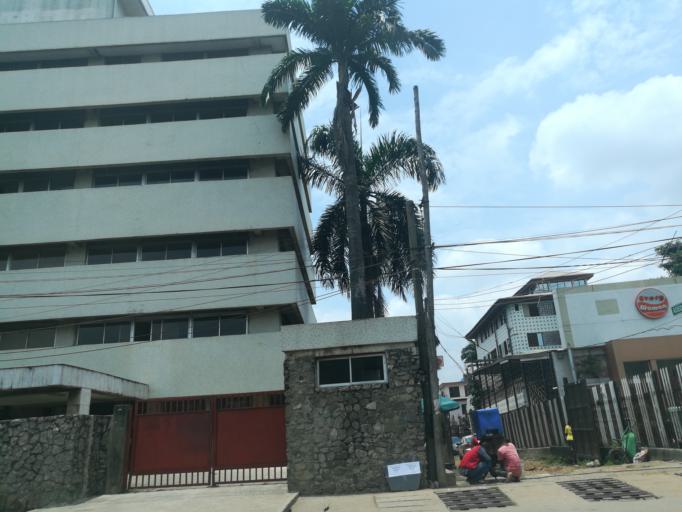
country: NG
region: Lagos
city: Ikeja
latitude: 6.5926
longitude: 3.3586
